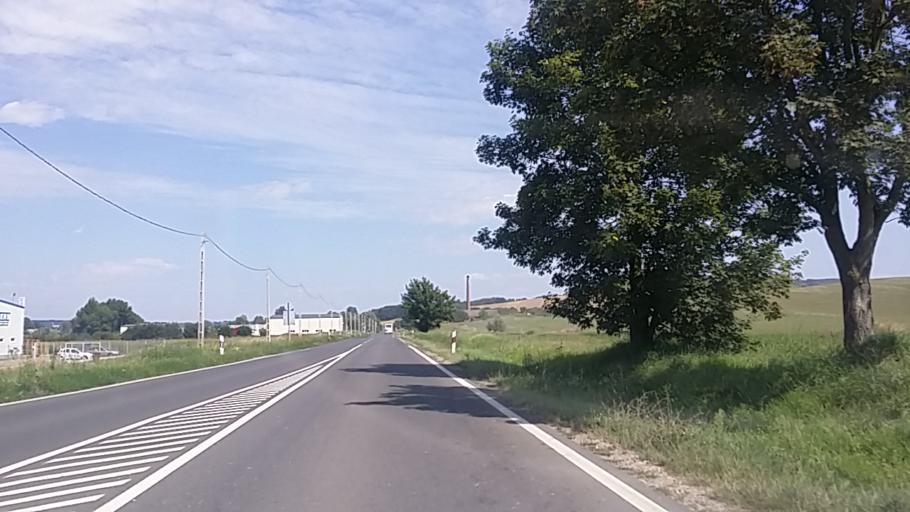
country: HU
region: Baranya
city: Sasd
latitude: 46.2397
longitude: 18.1209
